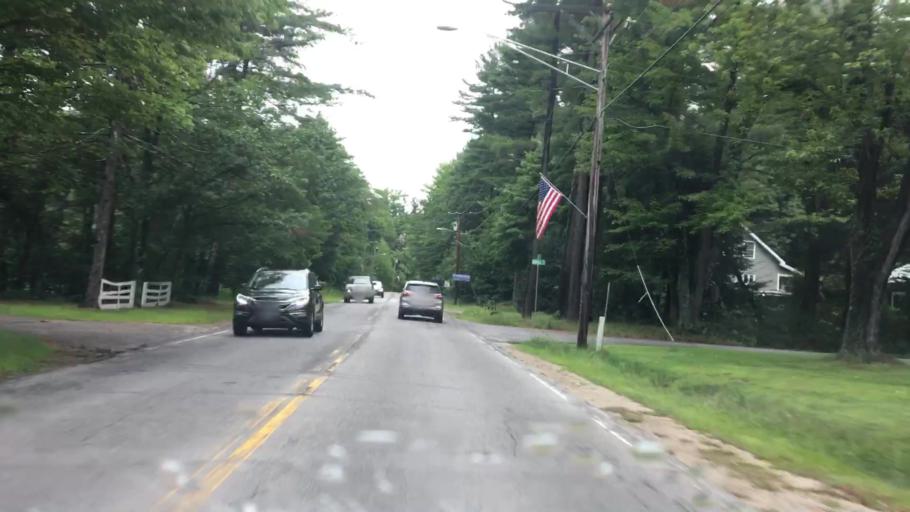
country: US
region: Maine
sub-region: Oxford County
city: Fryeburg
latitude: 44.0099
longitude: -70.9874
